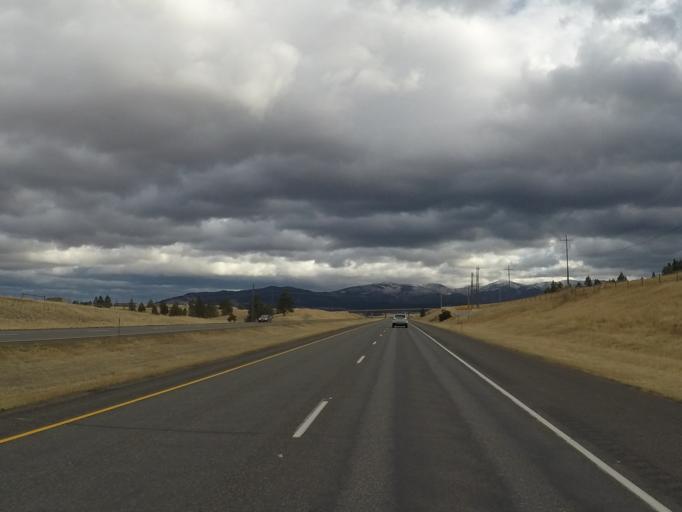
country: US
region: Montana
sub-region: Jefferson County
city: Montana City
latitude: 46.5671
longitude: -111.9638
